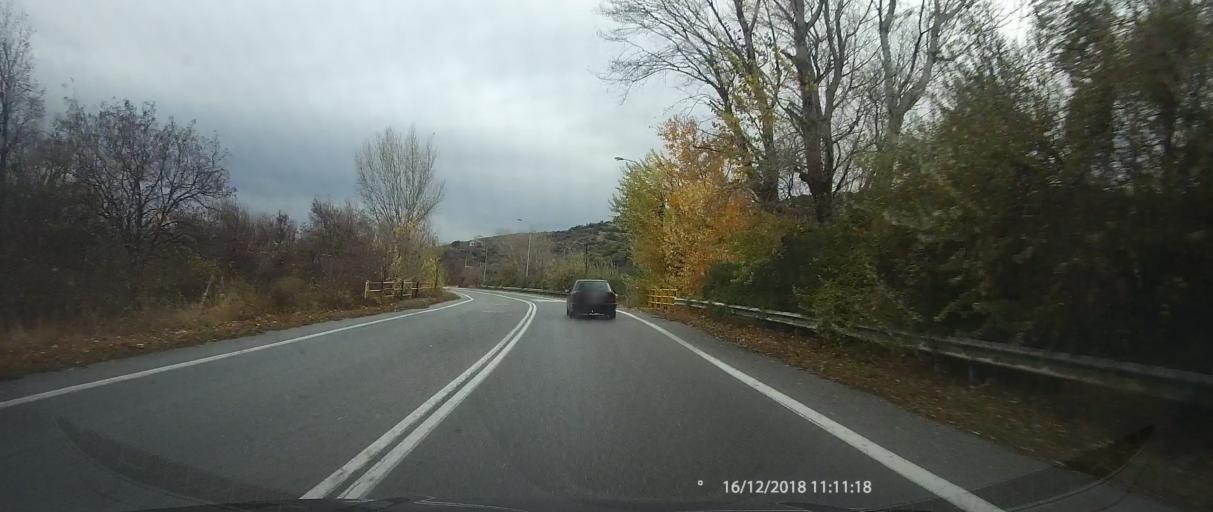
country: GR
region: East Macedonia and Thrace
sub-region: Nomos Xanthis
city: Petrochori
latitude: 41.0866
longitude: 24.7658
